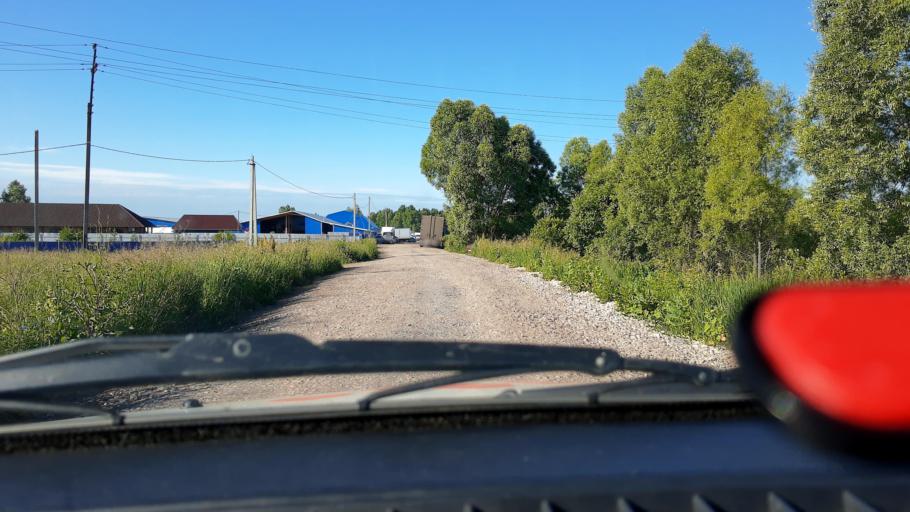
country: RU
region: Bashkortostan
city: Kabakovo
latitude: 54.7448
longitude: 56.2084
